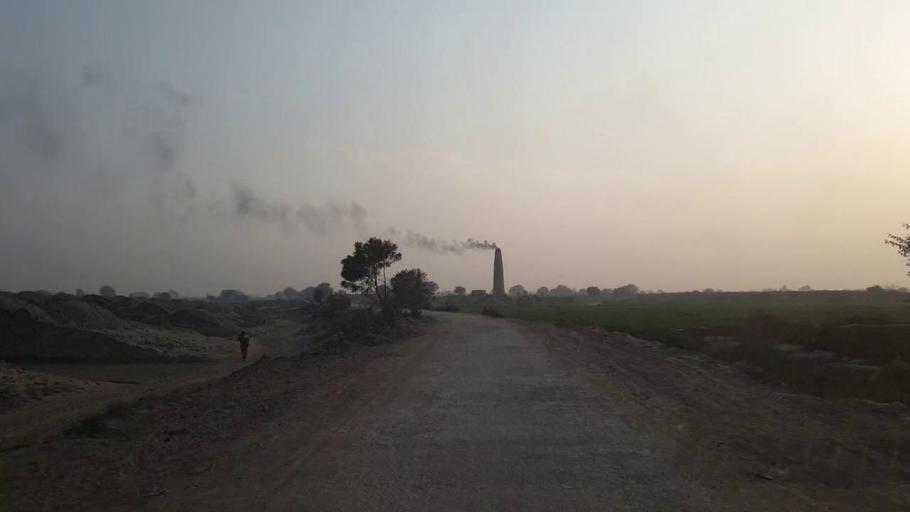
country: PK
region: Sindh
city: Bhit Shah
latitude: 25.7804
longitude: 68.4628
